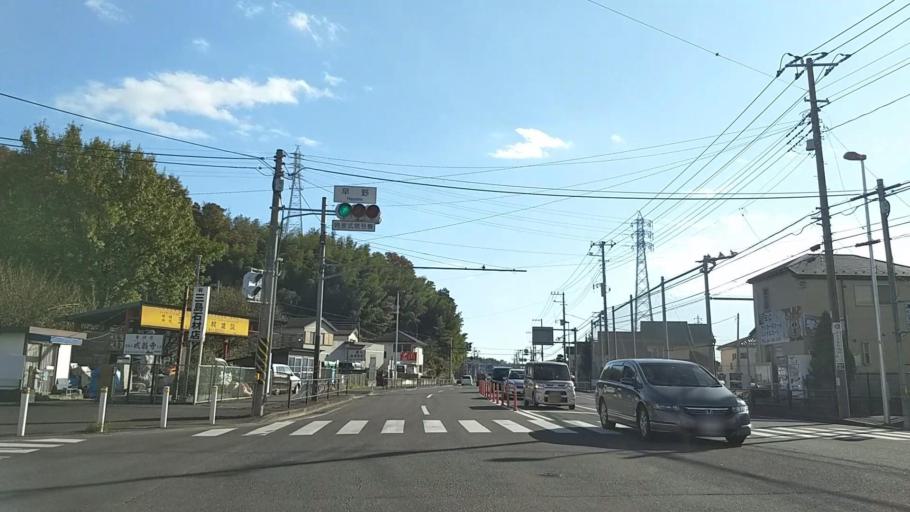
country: JP
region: Tokyo
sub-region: Machida-shi
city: Machida
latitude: 35.5696
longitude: 139.5134
